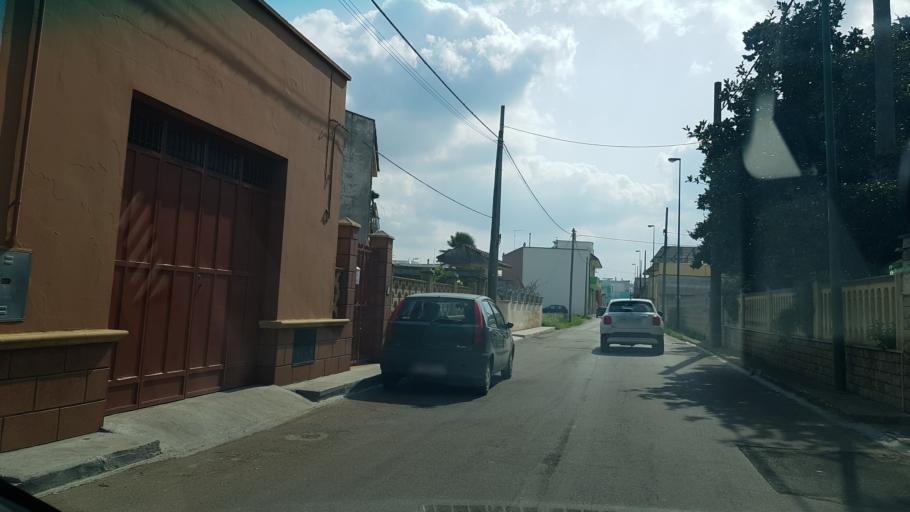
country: IT
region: Apulia
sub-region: Provincia di Brindisi
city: Torchiarolo
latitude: 40.4880
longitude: 18.0483
